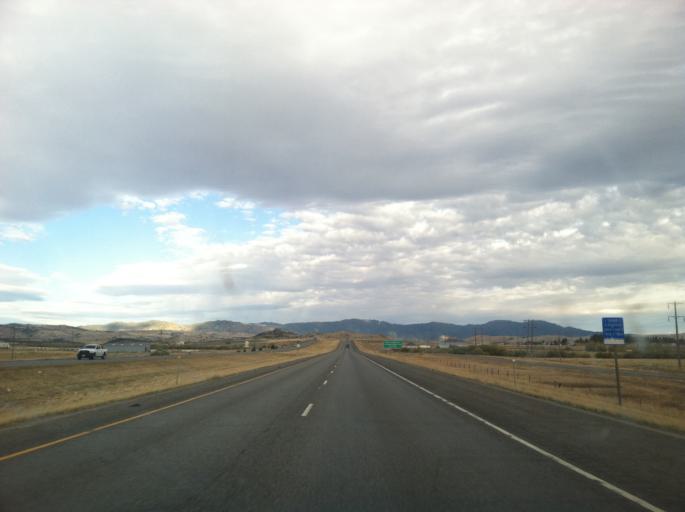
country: US
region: Montana
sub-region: Silver Bow County
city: Butte-Silver Bow (Balance)
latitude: 46.0100
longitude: -112.7005
